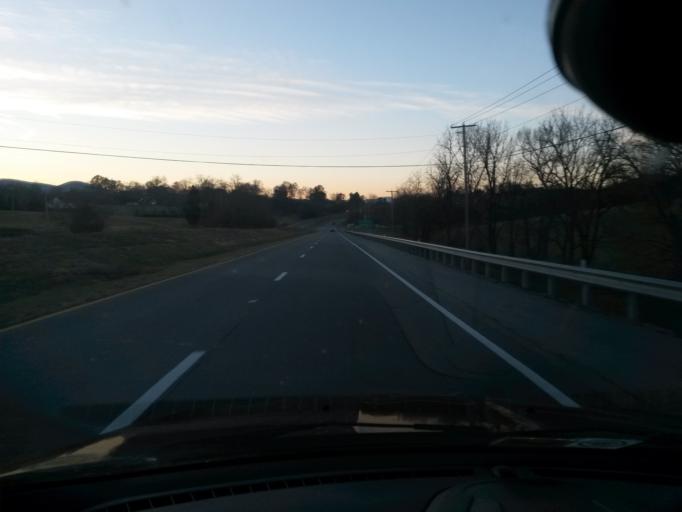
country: US
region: Virginia
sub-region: Botetourt County
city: Daleville
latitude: 37.4408
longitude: -79.9043
